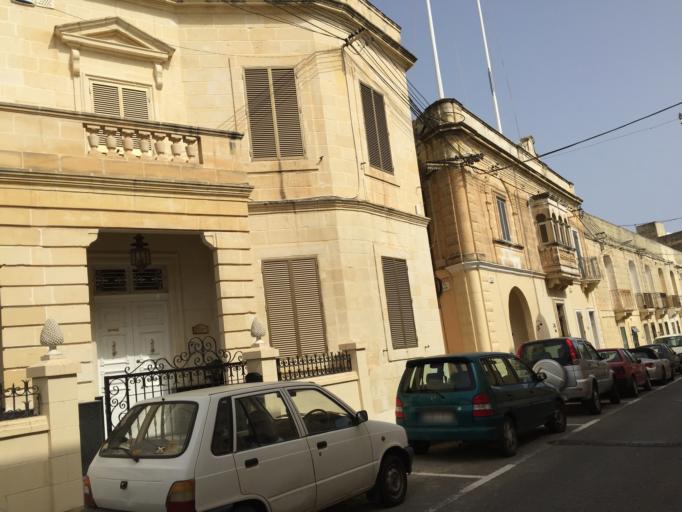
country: MT
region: Bormla
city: Cospicua
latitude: 35.8909
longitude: 14.5267
